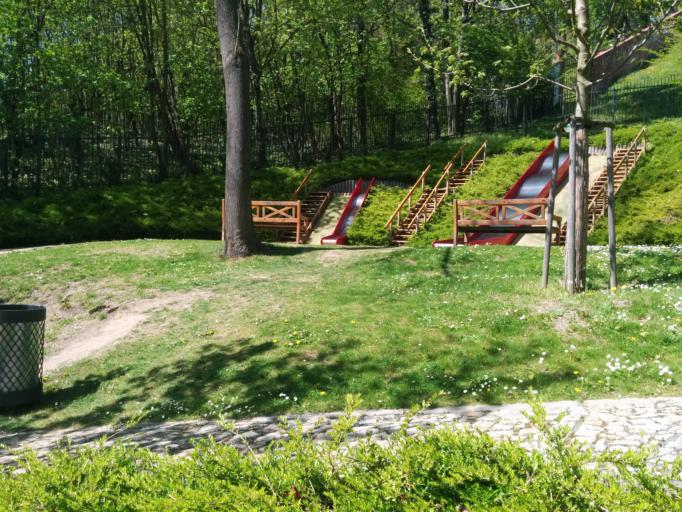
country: CZ
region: Praha
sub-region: Praha 1
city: Mala Strana
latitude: 50.0779
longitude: 14.3971
